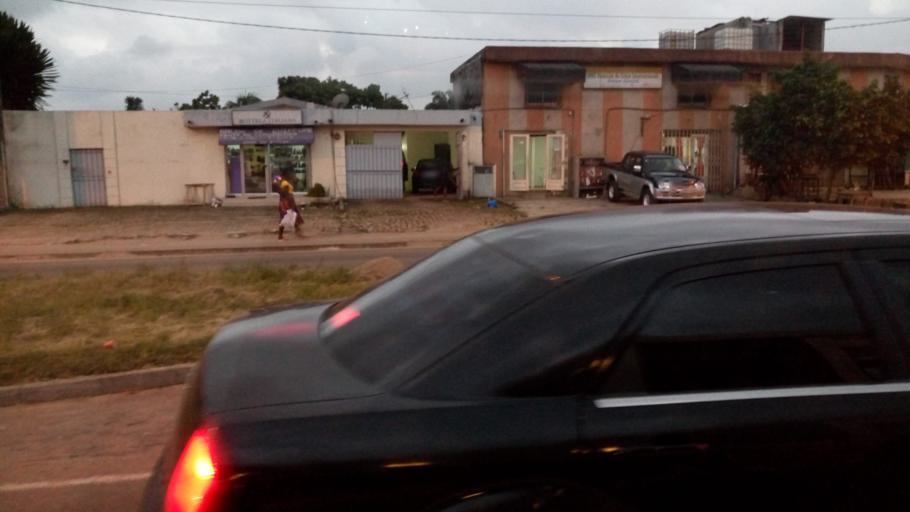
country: CI
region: Lagunes
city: Abobo
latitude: 5.3912
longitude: -3.9922
